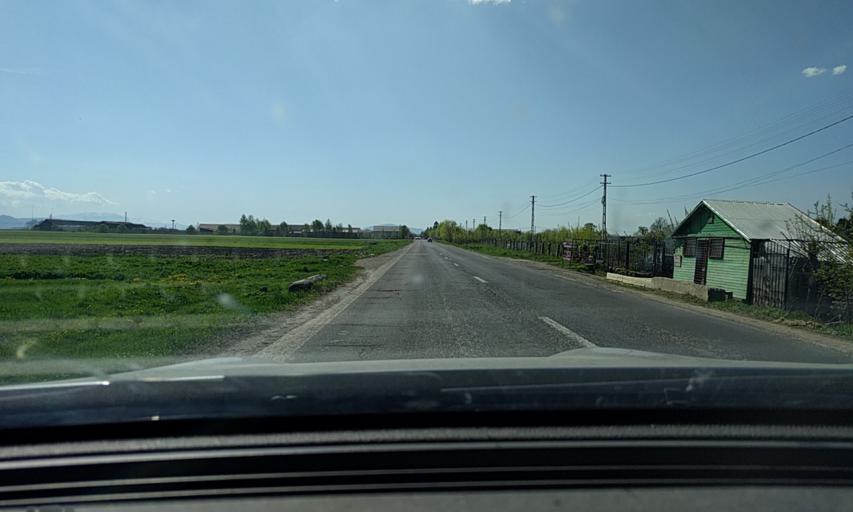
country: RO
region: Brasov
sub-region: Comuna Prejmer
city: Prejmer
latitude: 45.7136
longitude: 25.7892
